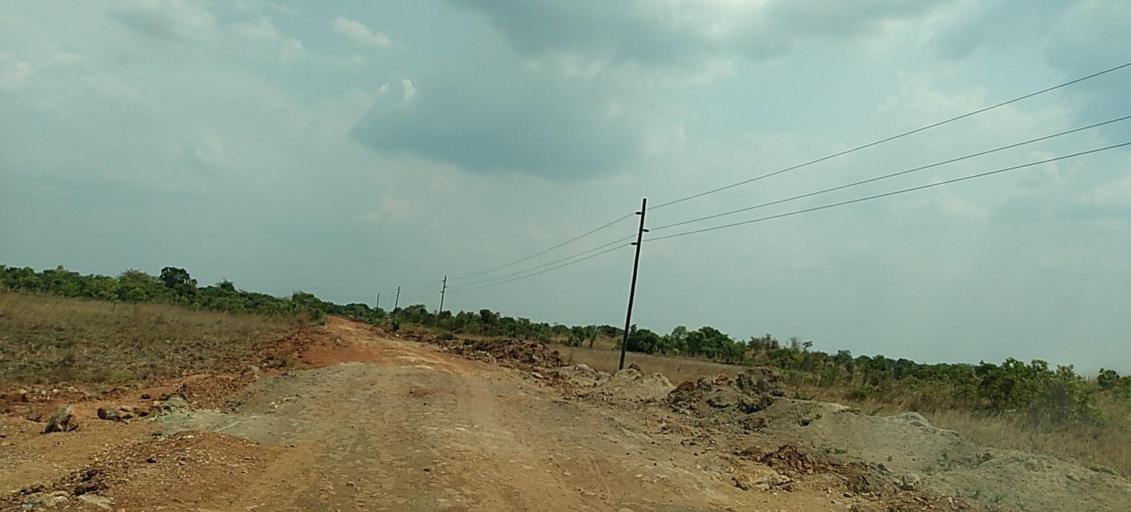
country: ZM
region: Copperbelt
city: Kalulushi
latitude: -12.8867
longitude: 28.0747
